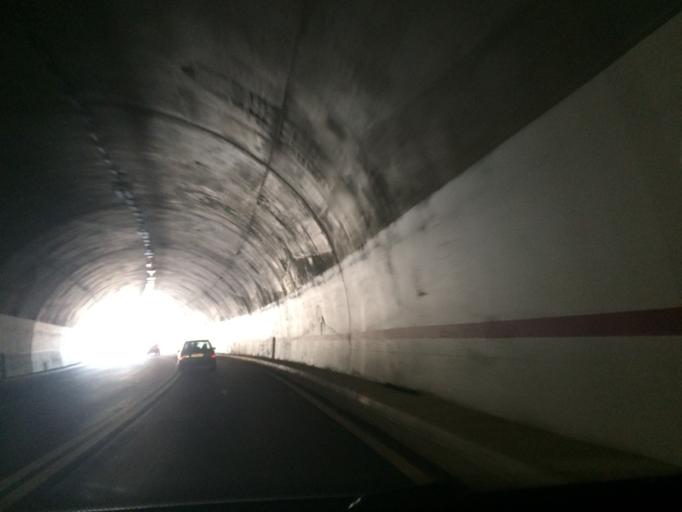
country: ME
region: Cetinje
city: Cetinje
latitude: 42.3789
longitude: 18.9736
